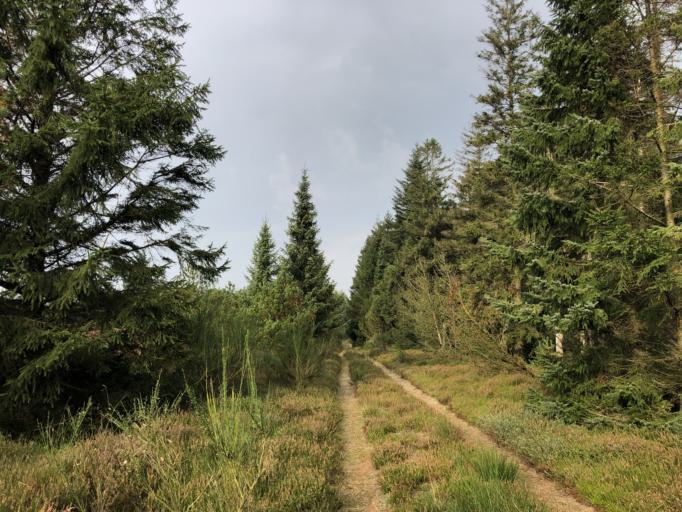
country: DK
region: Central Jutland
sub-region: Holstebro Kommune
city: Ulfborg
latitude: 56.2492
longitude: 8.4572
